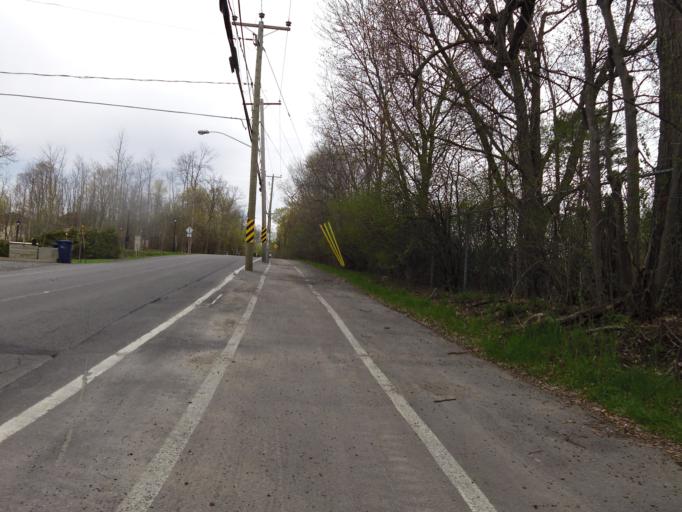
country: CA
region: Quebec
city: Dollard-Des Ormeaux
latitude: 45.5221
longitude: -73.8411
